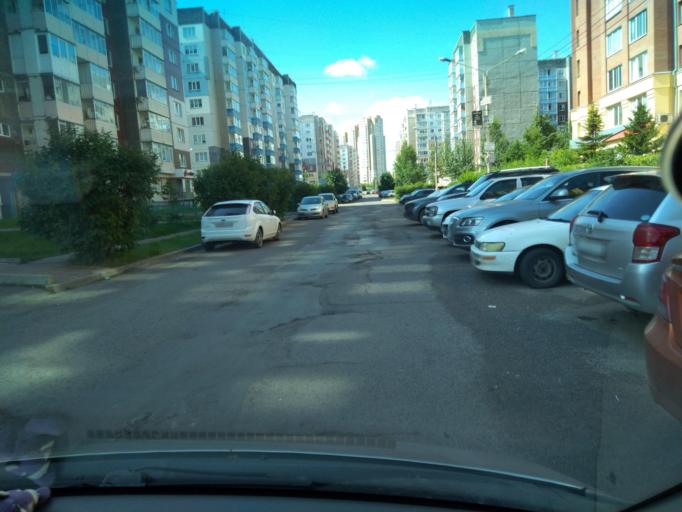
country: RU
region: Krasnoyarskiy
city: Krasnoyarsk
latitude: 56.0436
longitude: 92.9013
